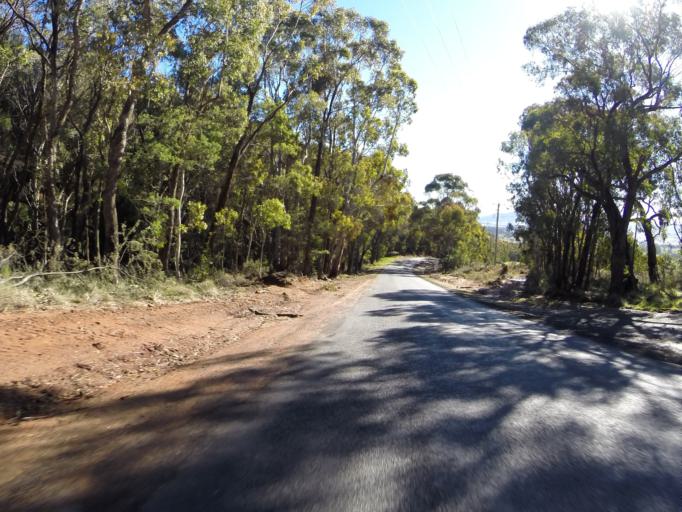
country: AU
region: New South Wales
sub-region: Oberon
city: Oberon
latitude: -33.6210
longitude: 149.8462
